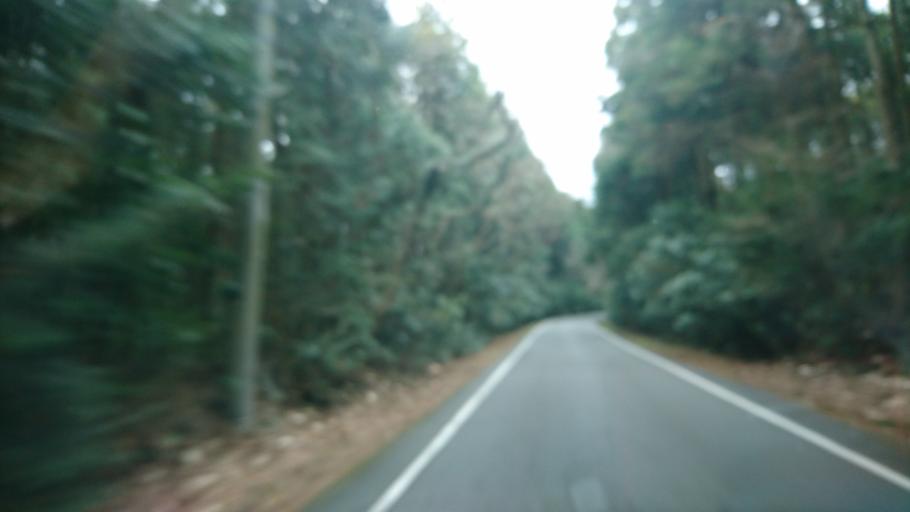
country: JP
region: Shizuoka
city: Fujinomiya
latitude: 35.3236
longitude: 138.5740
